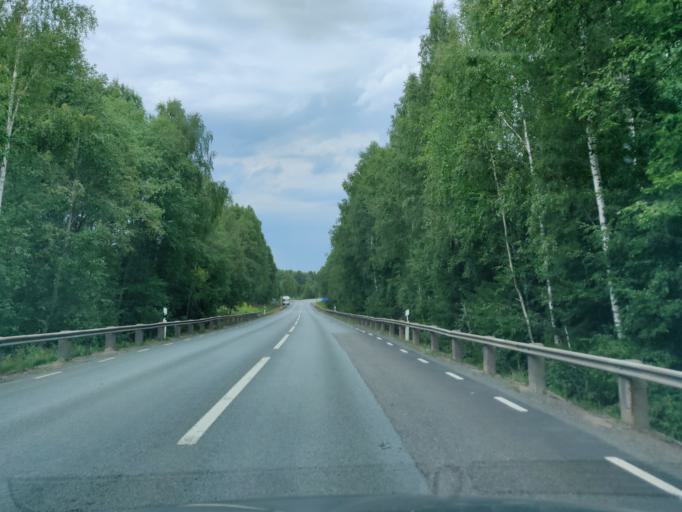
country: SE
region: Vaermland
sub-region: Munkfors Kommun
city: Munkfors
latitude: 59.8581
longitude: 13.5620
